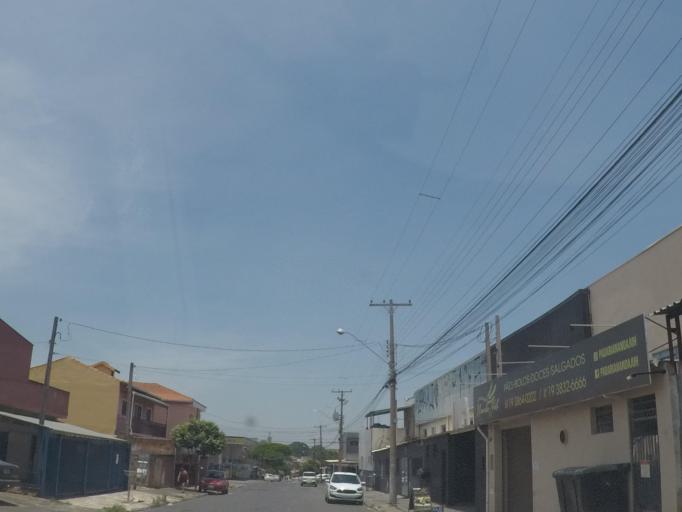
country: BR
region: Sao Paulo
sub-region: Hortolandia
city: Hortolandia
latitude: -22.8510
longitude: -47.1886
